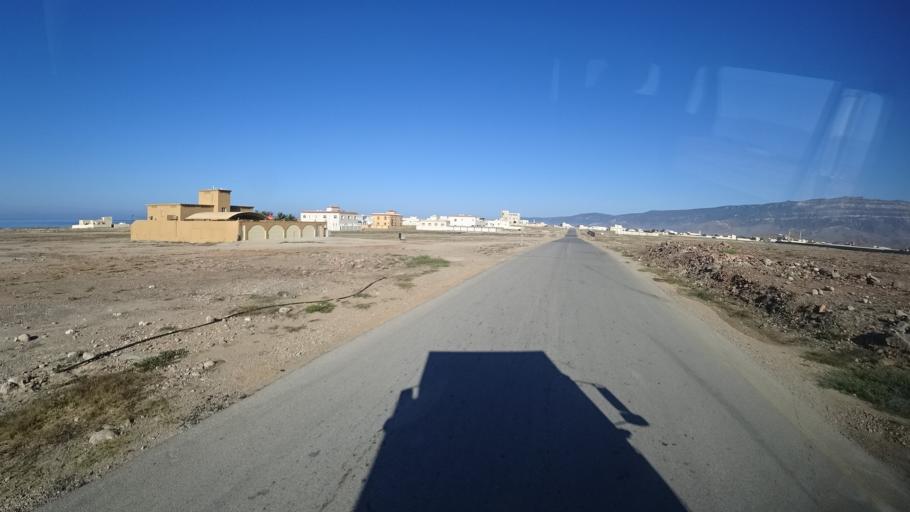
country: OM
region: Zufar
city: Salalah
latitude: 16.9778
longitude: 54.7011
